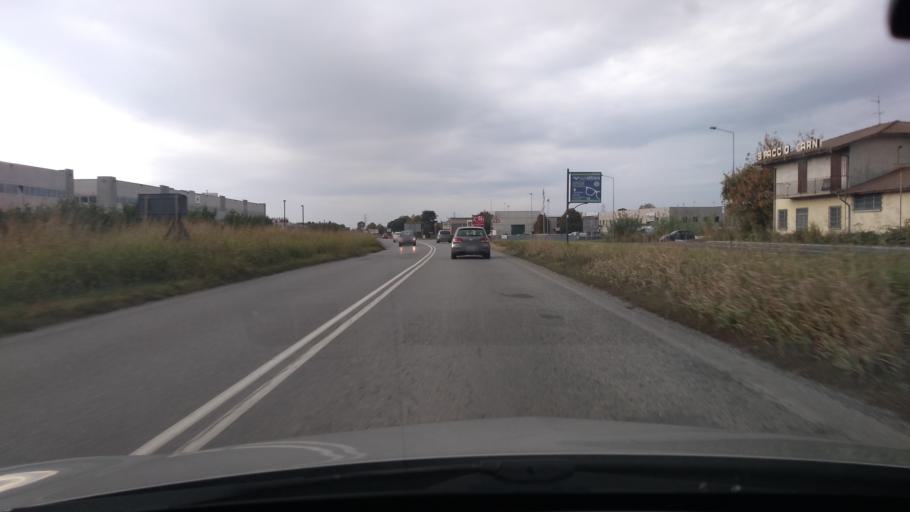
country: IT
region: Lombardy
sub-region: Provincia di Bergamo
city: Pognano
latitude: 45.5936
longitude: 9.6505
